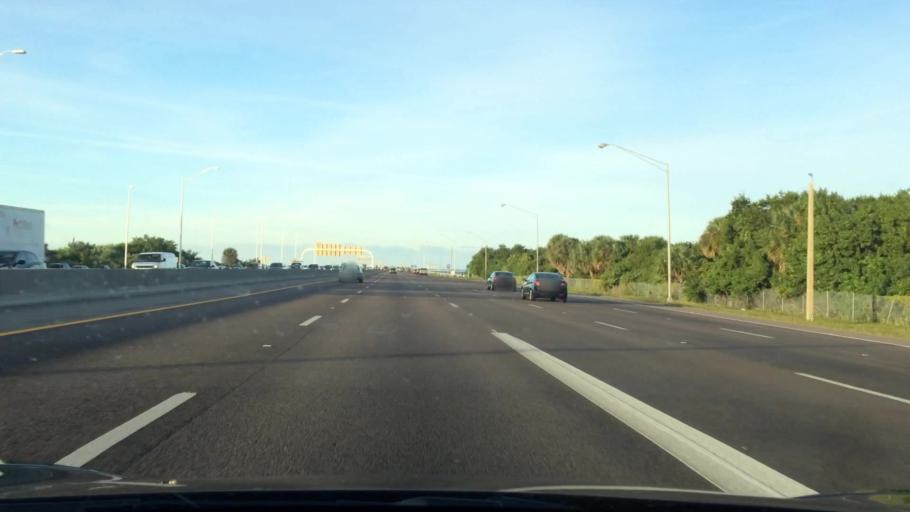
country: US
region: Florida
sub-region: Hillsborough County
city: Town 'n' Country
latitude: 27.9433
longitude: -82.5448
